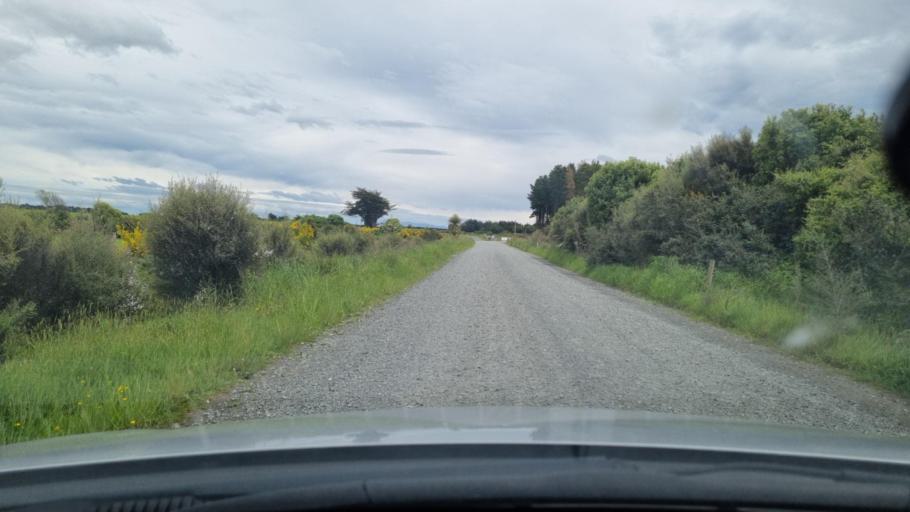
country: NZ
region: Southland
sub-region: Invercargill City
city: Invercargill
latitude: -46.4066
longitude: 168.2759
